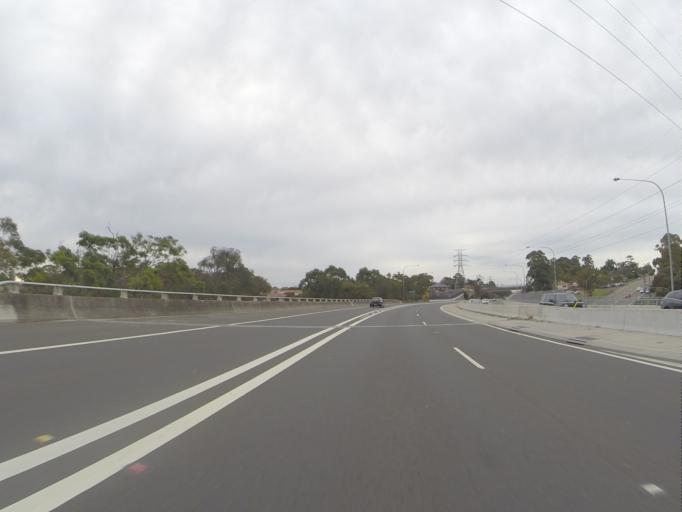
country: AU
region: New South Wales
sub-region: Bankstown
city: Padstow
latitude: -33.9646
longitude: 151.0350
